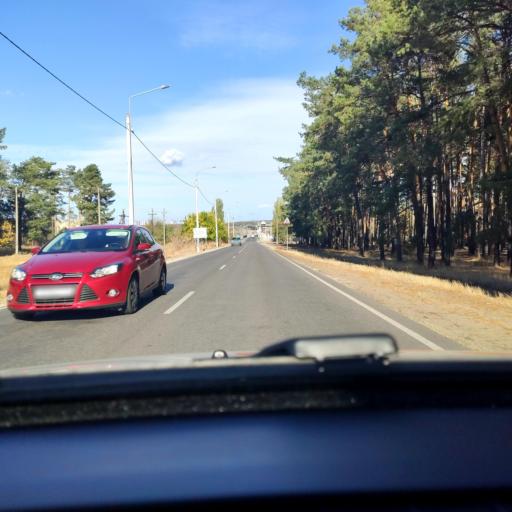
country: RU
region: Voronezj
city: Shilovo
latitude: 51.5347
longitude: 39.1396
